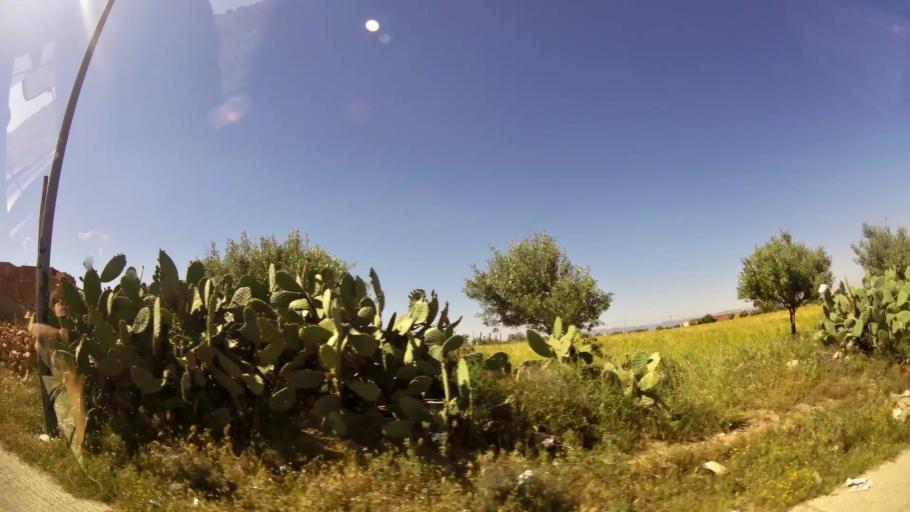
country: MA
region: Oriental
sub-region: Oujda-Angad
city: Oujda
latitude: 34.6958
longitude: -1.8591
